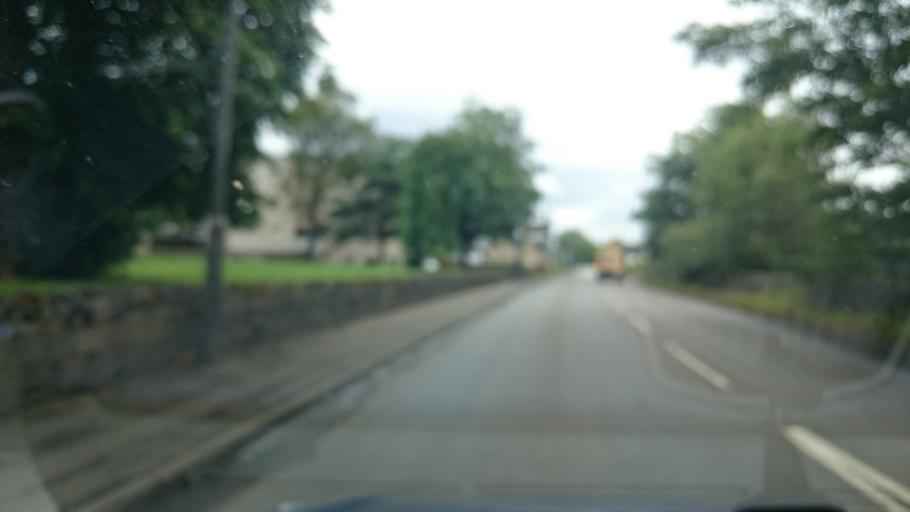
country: GB
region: Scotland
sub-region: Falkirk
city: Bonnybridge
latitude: 56.0022
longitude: -3.8968
